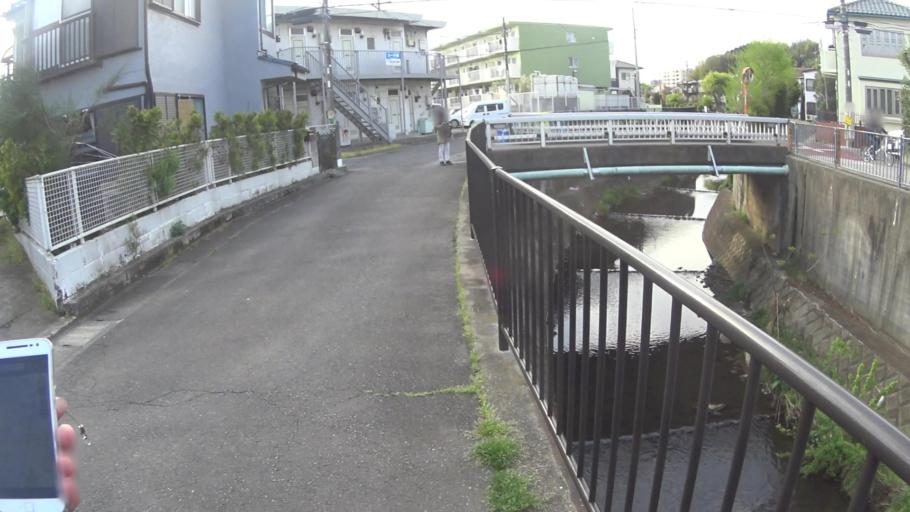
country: JP
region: Tokyo
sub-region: Machida-shi
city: Machida
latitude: 35.5831
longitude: 139.4890
